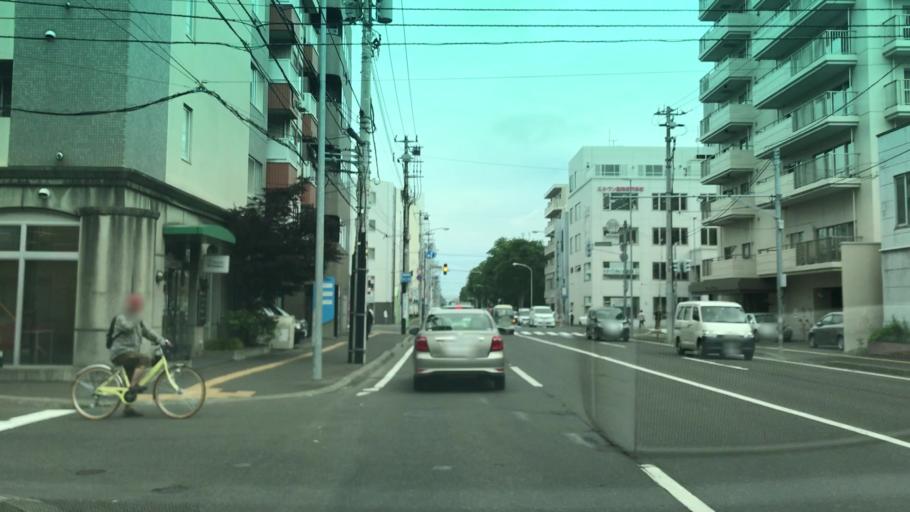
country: JP
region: Hokkaido
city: Sapporo
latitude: 43.0579
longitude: 141.3270
